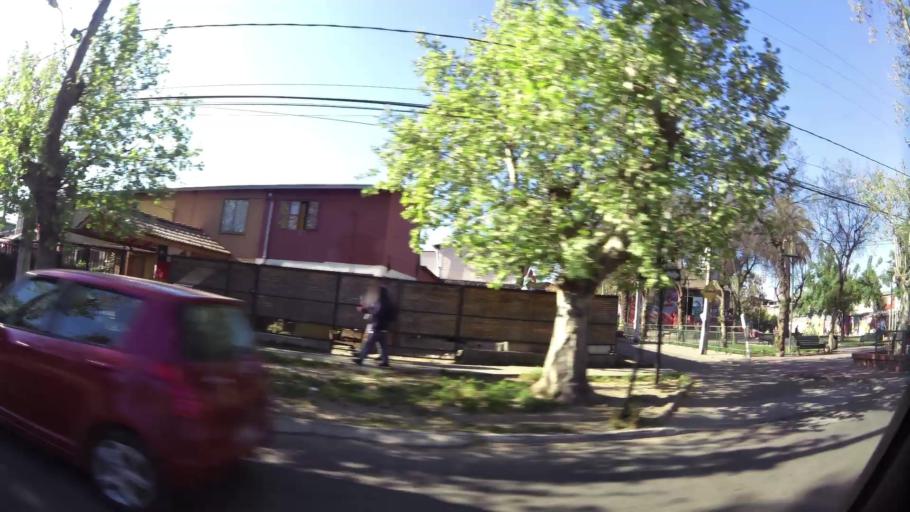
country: CL
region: Santiago Metropolitan
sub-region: Provincia de Talagante
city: Penaflor
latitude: -33.6062
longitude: -70.8625
